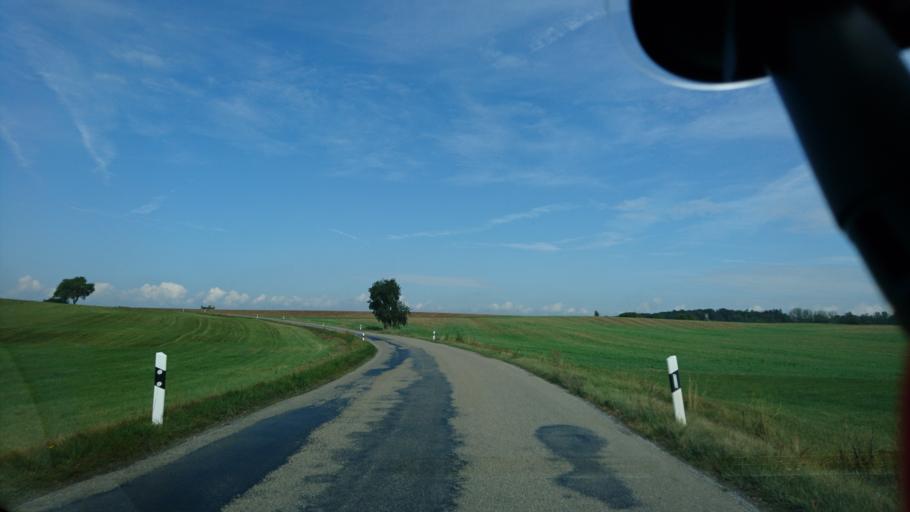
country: DE
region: Baden-Wuerttemberg
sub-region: Regierungsbezirk Stuttgart
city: Ilshofen
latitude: 49.1372
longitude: 9.9300
